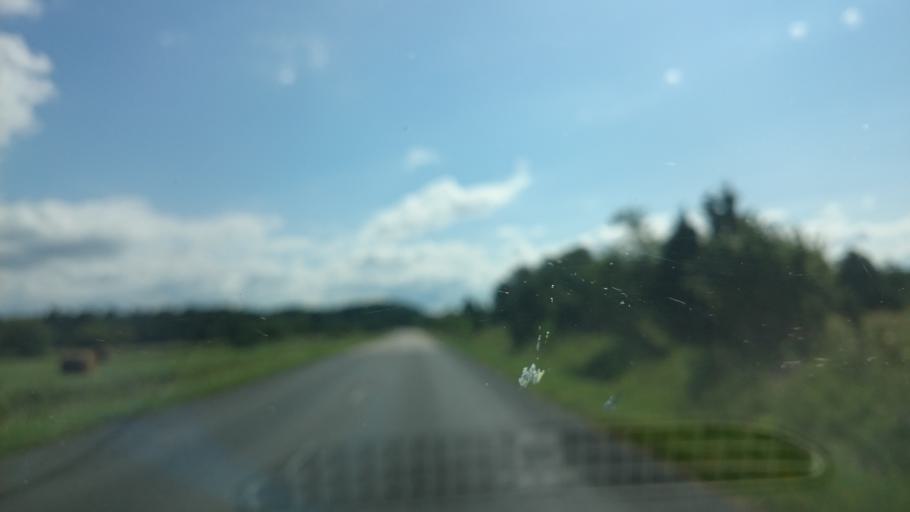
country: EE
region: Saare
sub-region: Orissaare vald
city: Orissaare
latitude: 58.5752
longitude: 22.7626
